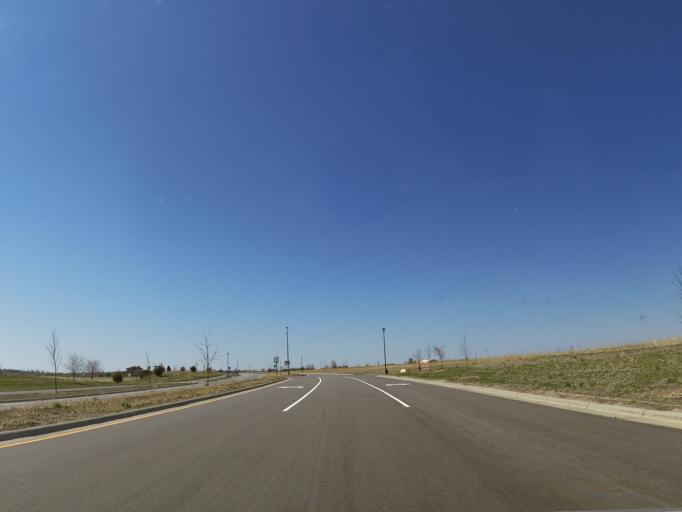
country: US
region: Minnesota
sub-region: Scott County
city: Prior Lake
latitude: 44.7631
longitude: -93.4432
